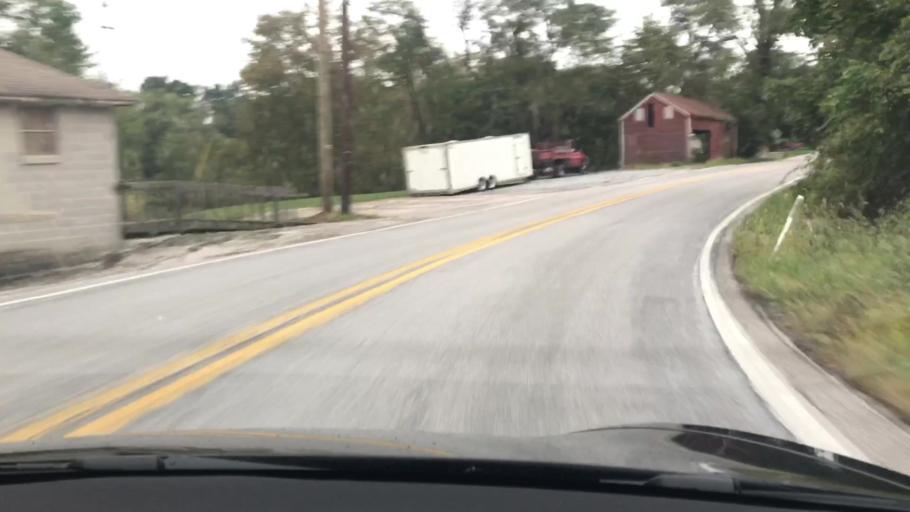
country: US
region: Pennsylvania
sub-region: York County
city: Weigelstown
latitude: 39.9431
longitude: -76.8624
